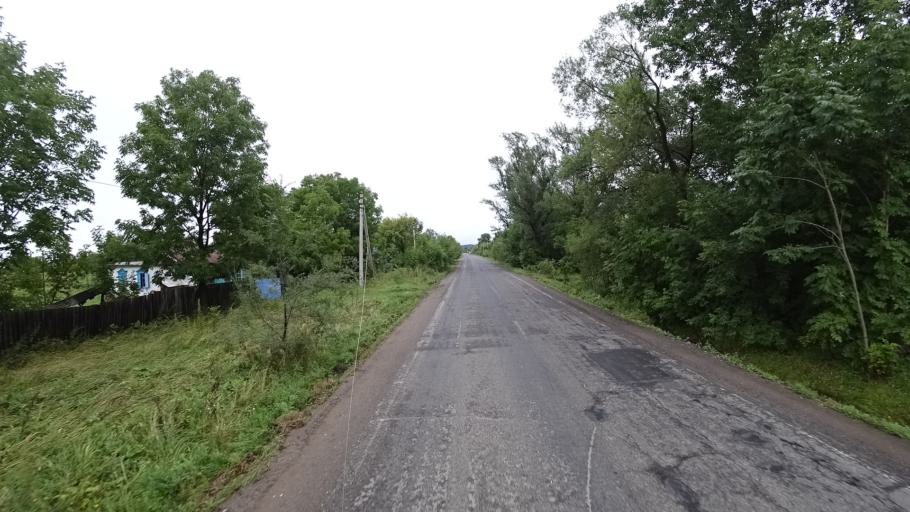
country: RU
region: Primorskiy
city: Monastyrishche
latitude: 44.1921
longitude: 132.4891
